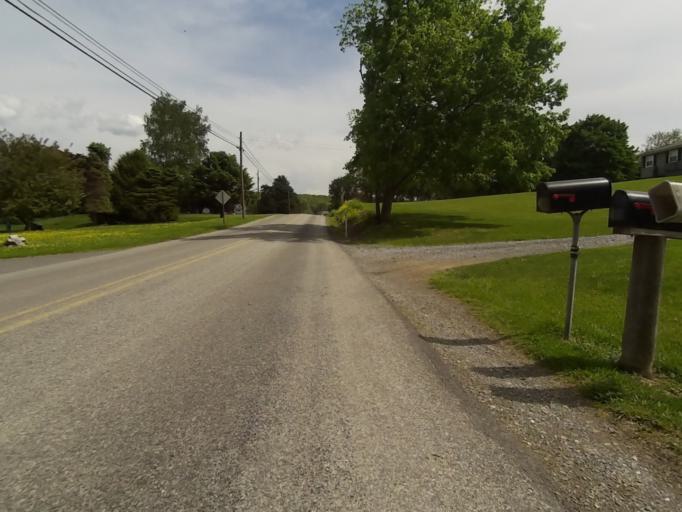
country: US
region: Pennsylvania
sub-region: Centre County
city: Zion
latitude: 40.9831
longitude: -77.6311
